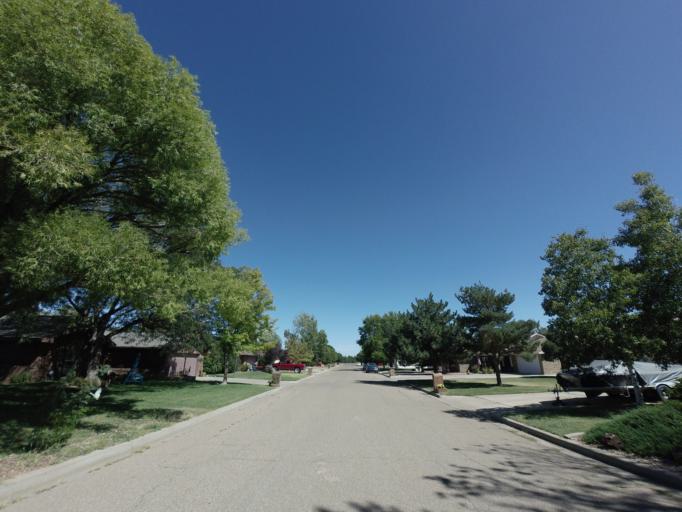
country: US
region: New Mexico
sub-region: Curry County
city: Clovis
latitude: 34.4448
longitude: -103.1813
